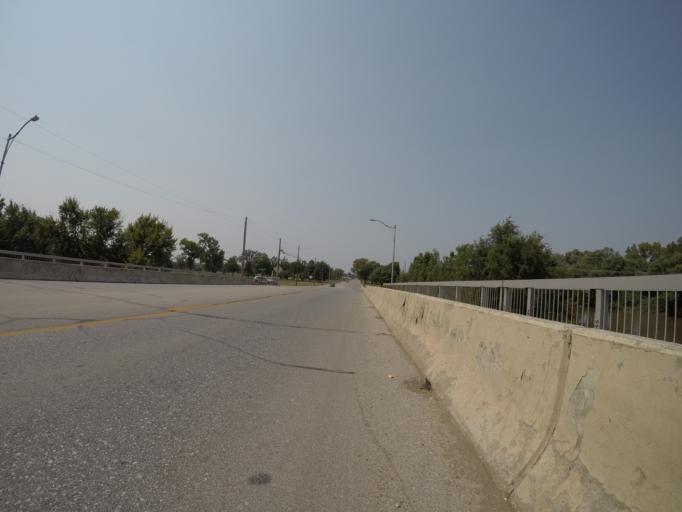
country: US
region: Nebraska
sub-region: Gage County
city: Beatrice
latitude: 40.2660
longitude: -96.7542
